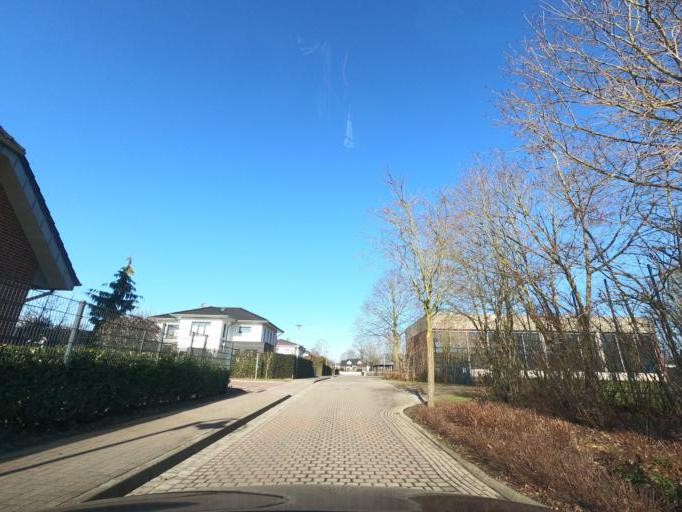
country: DE
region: Lower Saxony
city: Emstek
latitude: 52.8578
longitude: 8.1277
